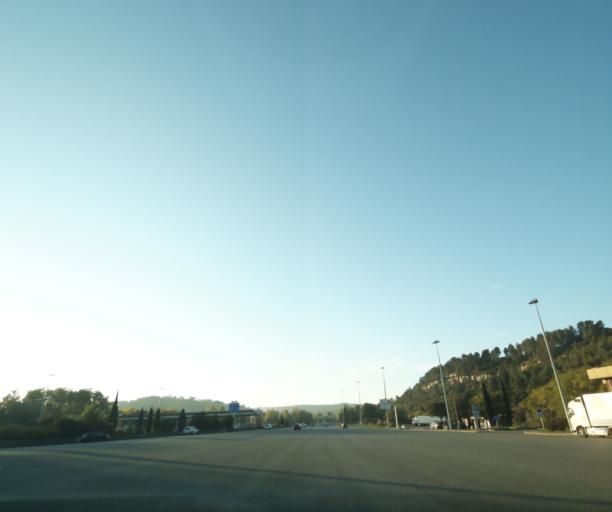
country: FR
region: Provence-Alpes-Cote d'Azur
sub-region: Departement des Bouches-du-Rhone
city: Chateauneuf-le-Rouge
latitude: 43.4832
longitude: 5.5404
